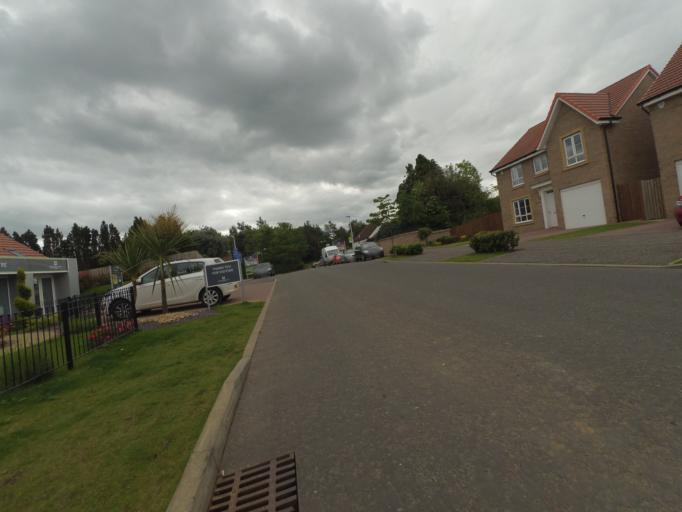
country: GB
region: Scotland
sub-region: East Lothian
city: Musselburgh
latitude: 55.9357
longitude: -3.0905
